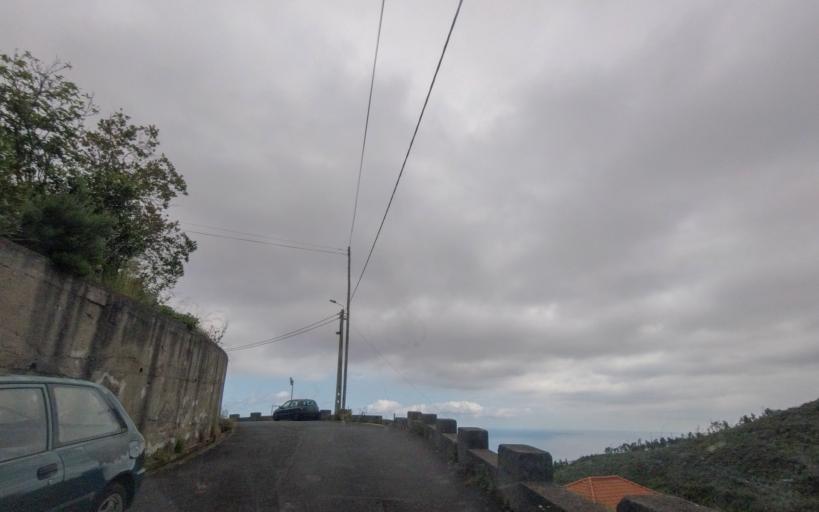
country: PT
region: Madeira
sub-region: Funchal
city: Nossa Senhora do Monte
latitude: 32.6792
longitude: -16.9139
